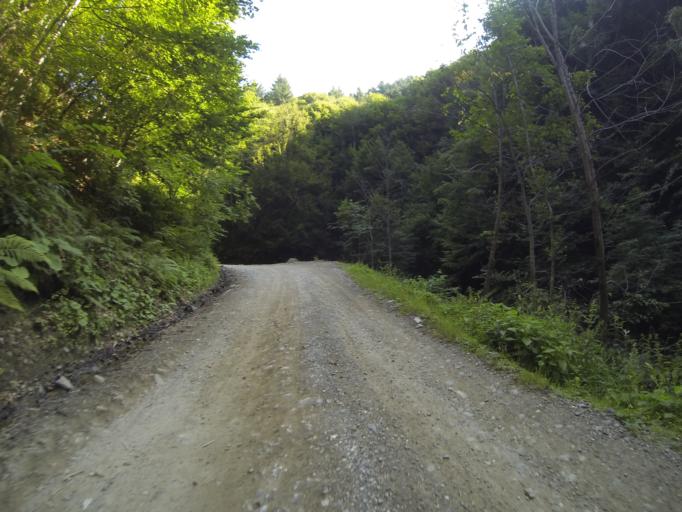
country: RO
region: Valcea
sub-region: Comuna Costesti
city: Bistrita
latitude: 45.2141
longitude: 24.0076
